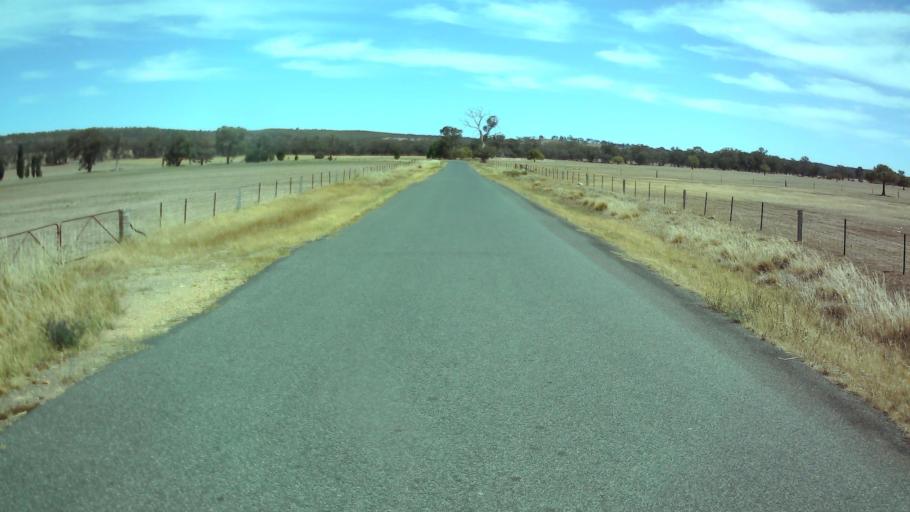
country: AU
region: New South Wales
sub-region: Weddin
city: Grenfell
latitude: -33.8399
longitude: 148.1772
